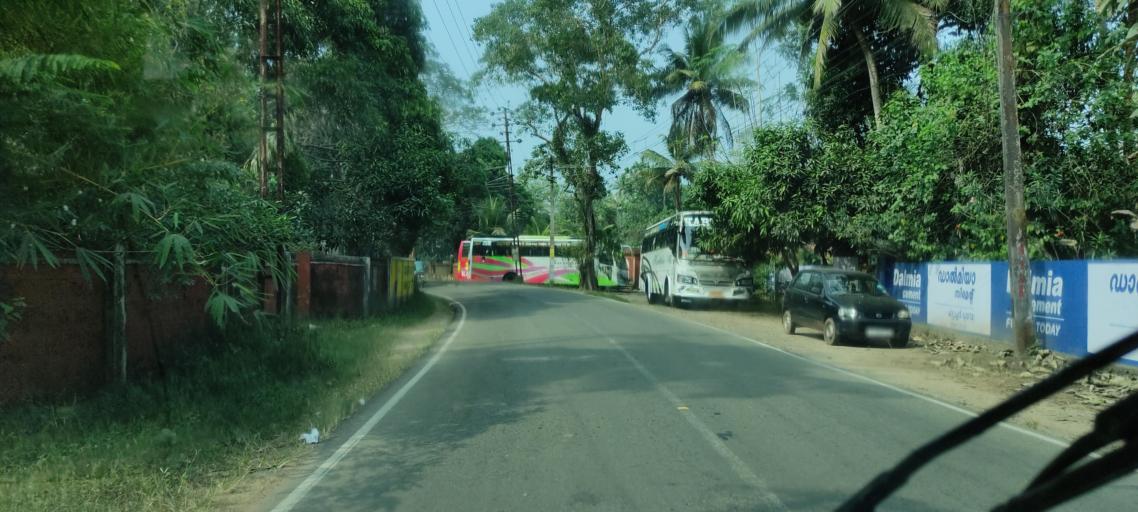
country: IN
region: Kerala
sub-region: Kottayam
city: Vaikam
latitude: 9.7295
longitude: 76.4147
